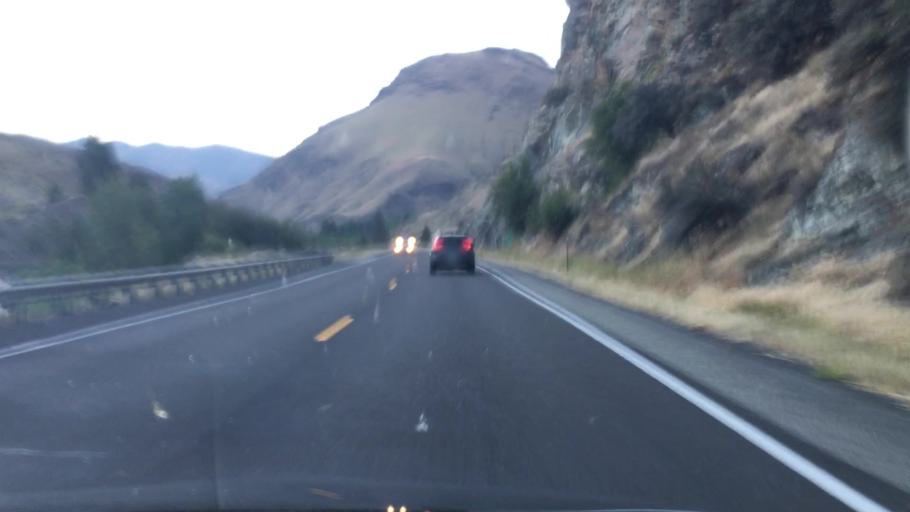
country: US
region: Idaho
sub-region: Valley County
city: McCall
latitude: 45.3303
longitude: -116.3472
